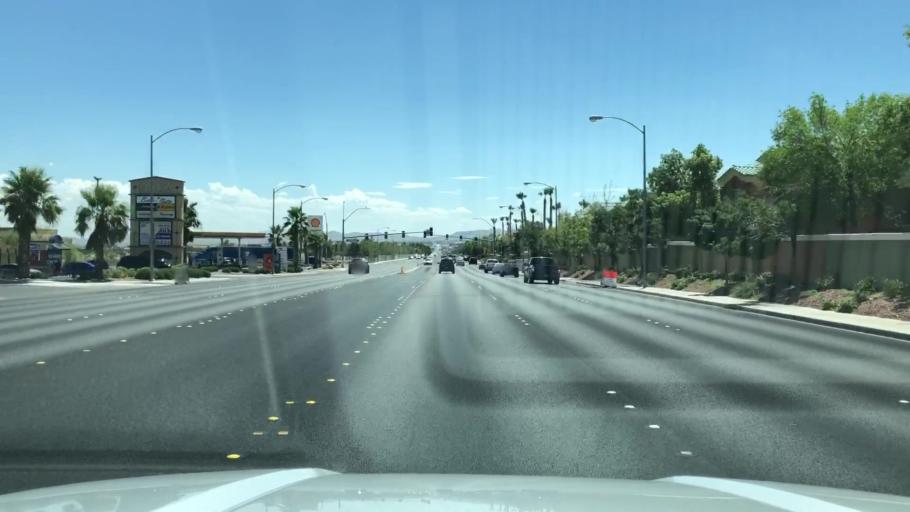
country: US
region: Nevada
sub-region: Clark County
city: Spring Valley
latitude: 36.1090
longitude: -115.2792
